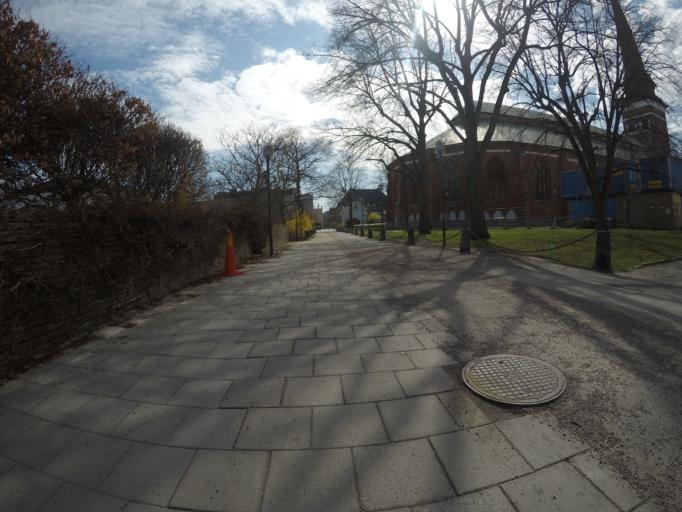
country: SE
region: Vaestmanland
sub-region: Vasteras
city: Vasteras
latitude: 59.6133
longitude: 16.5420
